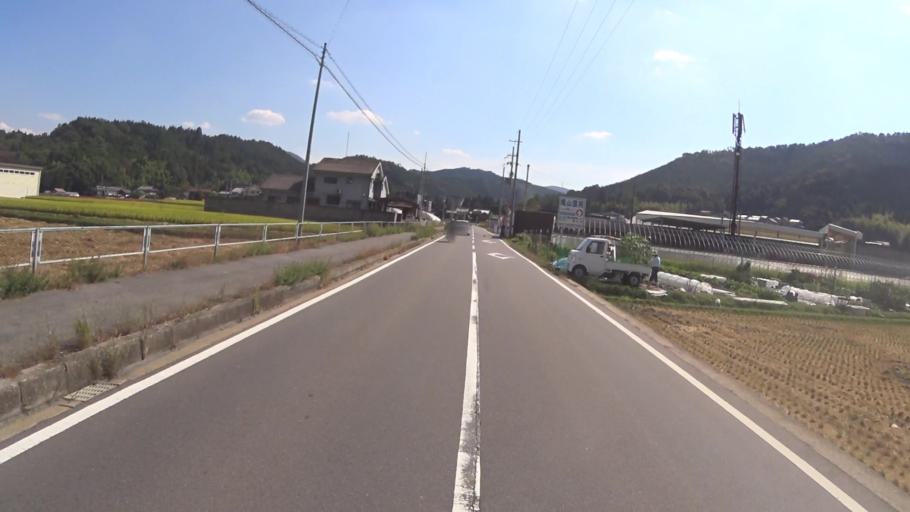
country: JP
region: Kyoto
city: Kameoka
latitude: 35.0004
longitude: 135.5781
